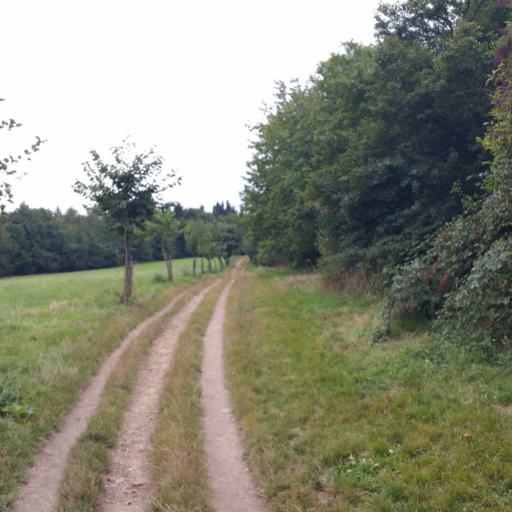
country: AT
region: Vienna
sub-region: Wien Stadt
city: Vienna
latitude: 48.2139
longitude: 16.2794
